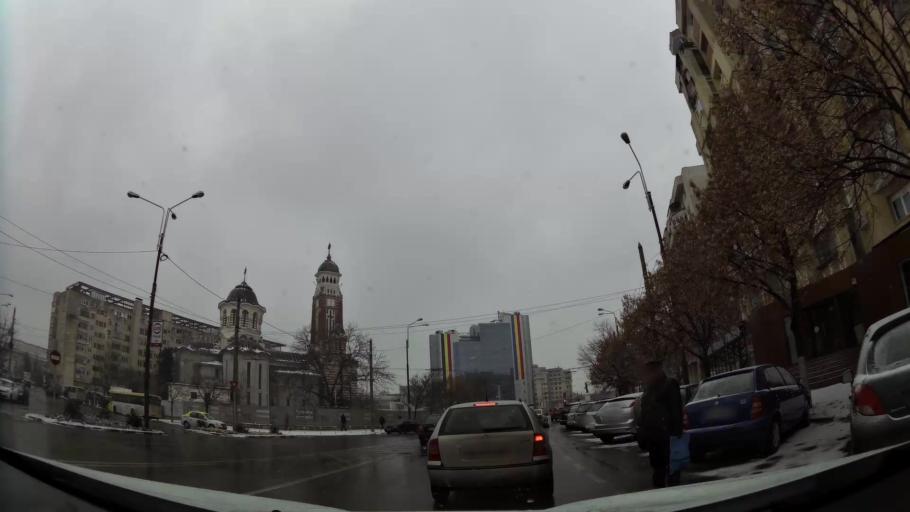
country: RO
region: Prahova
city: Ploiesti
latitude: 44.9442
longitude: 26.0189
